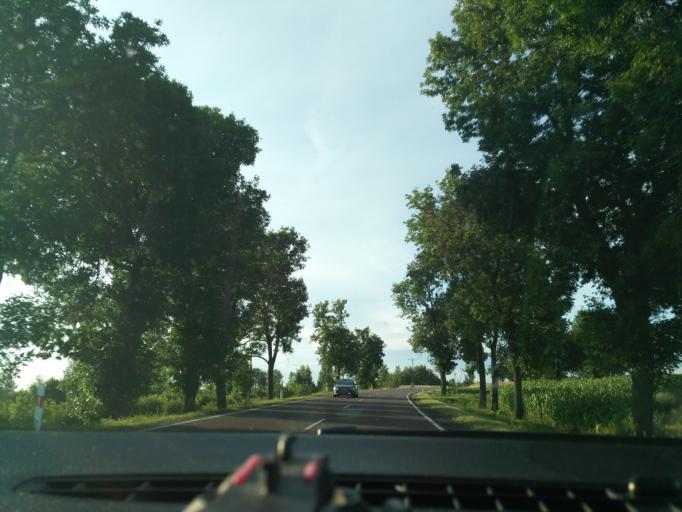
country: PL
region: Lublin Voivodeship
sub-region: Powiat krasnicki
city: Krasnik
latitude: 50.8835
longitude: 22.2608
